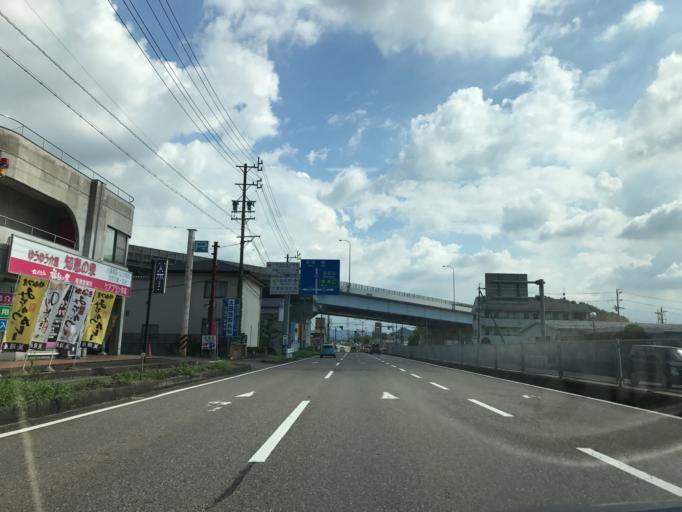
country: JP
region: Gifu
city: Mino
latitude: 35.5309
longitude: 136.9084
